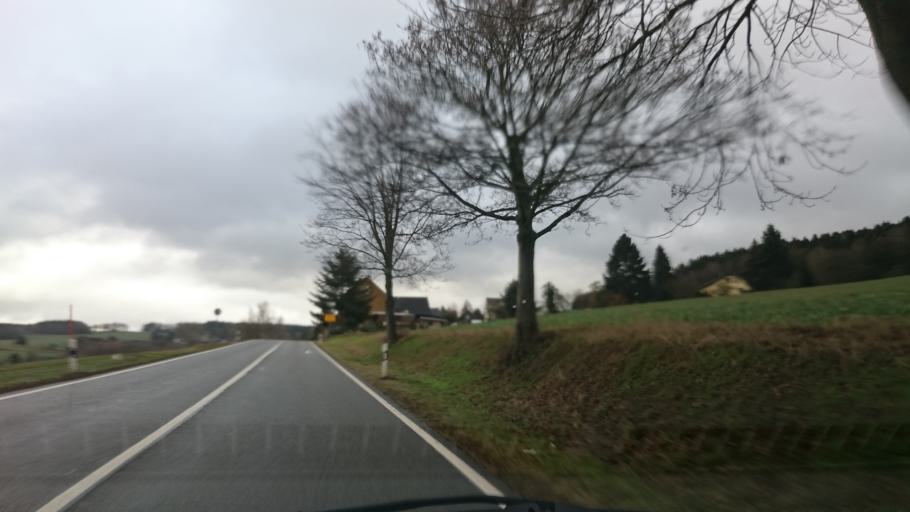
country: DE
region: Saxony
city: Kirchberg
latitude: 50.6238
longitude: 12.5743
